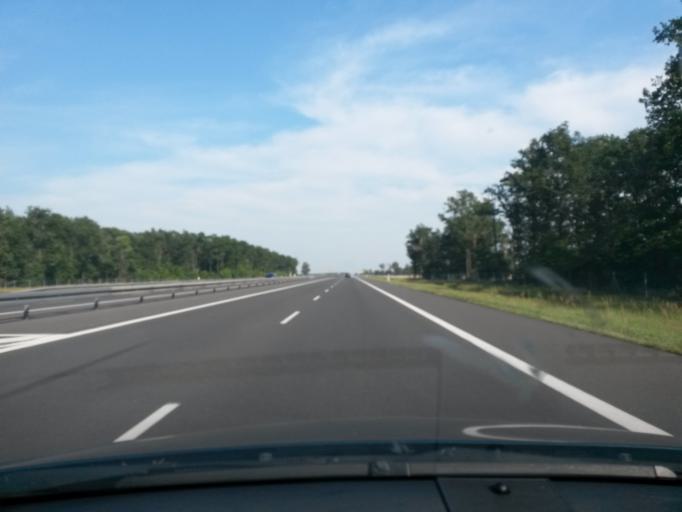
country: PL
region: Greater Poland Voivodeship
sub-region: Powiat wrzesinski
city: Wrzesnia
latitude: 52.3051
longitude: 17.6058
